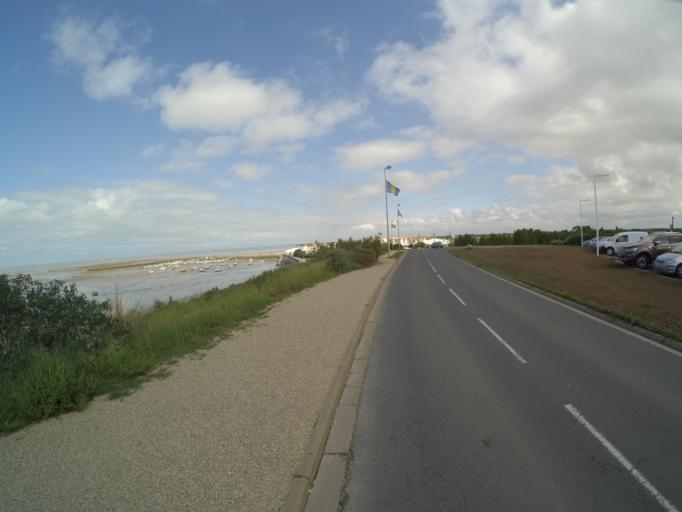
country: FR
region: Poitou-Charentes
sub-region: Departement de la Charente-Maritime
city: Chatelaillon-Plage
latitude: 46.0595
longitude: -1.0896
